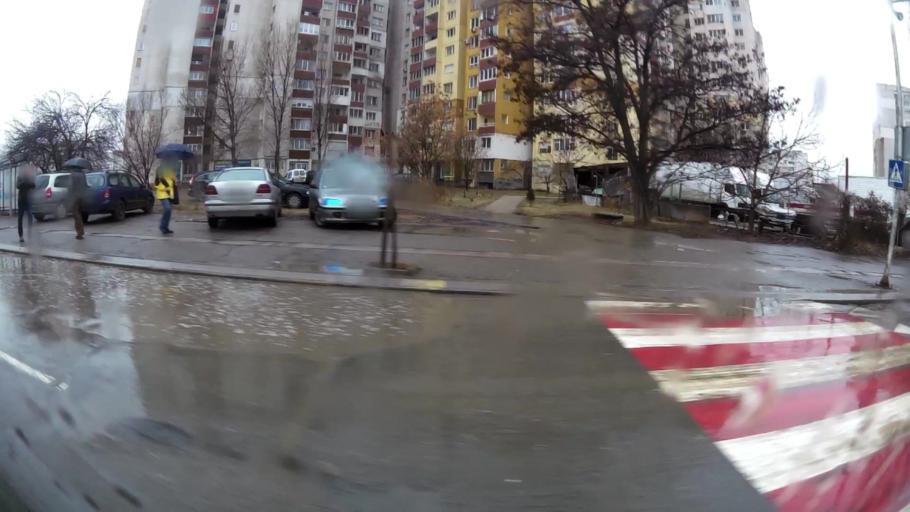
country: BG
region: Sofia-Capital
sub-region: Stolichna Obshtina
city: Sofia
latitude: 42.6491
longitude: 23.4087
